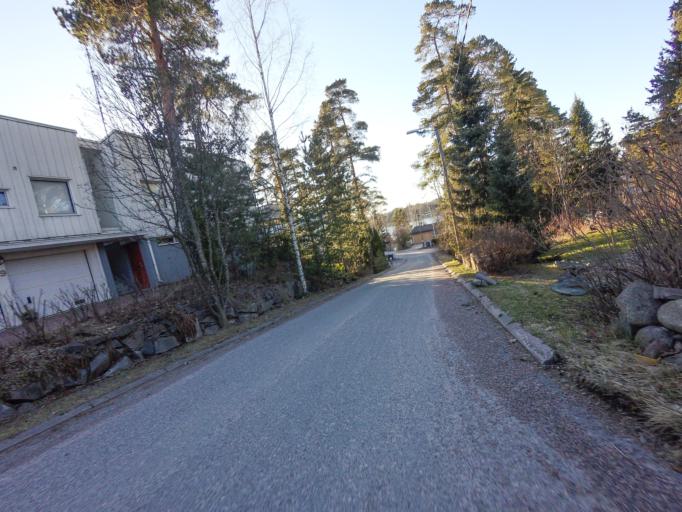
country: FI
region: Uusimaa
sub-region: Helsinki
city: Helsinki
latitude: 60.1755
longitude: 25.0214
